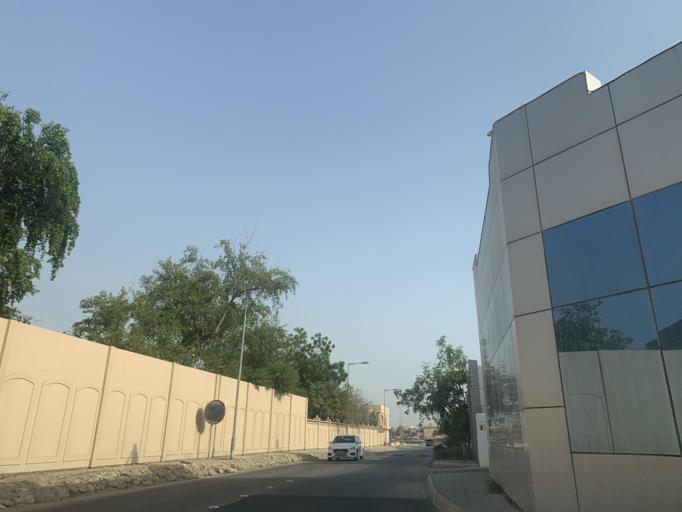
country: BH
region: Central Governorate
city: Madinat Hamad
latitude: 26.1748
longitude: 50.4697
